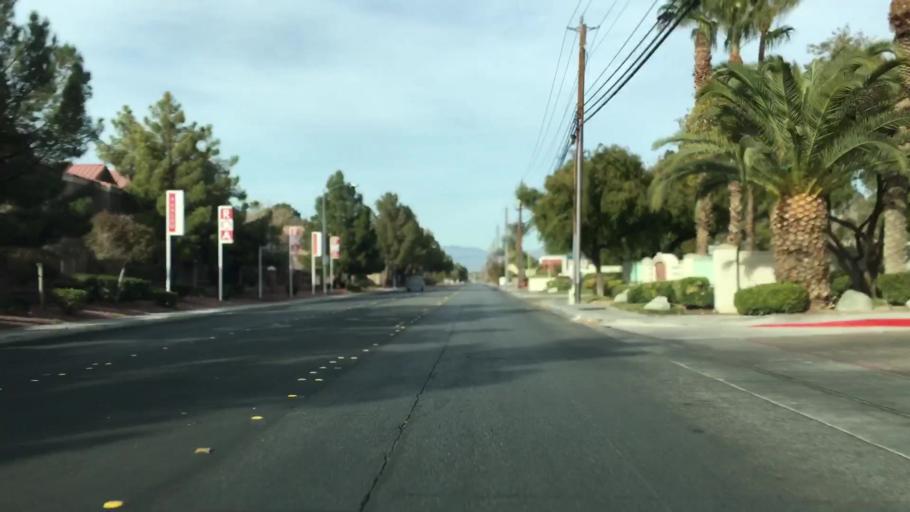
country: US
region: Nevada
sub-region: Clark County
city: Whitney
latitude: 36.0722
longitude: -115.0870
